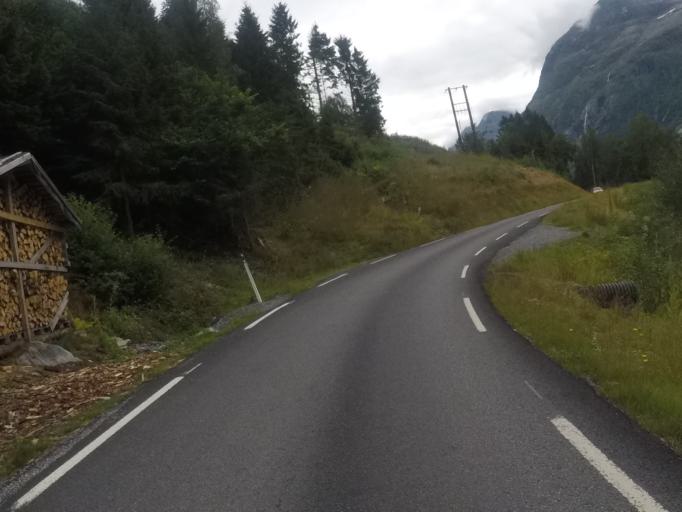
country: NO
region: Sogn og Fjordane
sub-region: Stryn
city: Stryn
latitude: 61.8404
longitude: 6.9454
